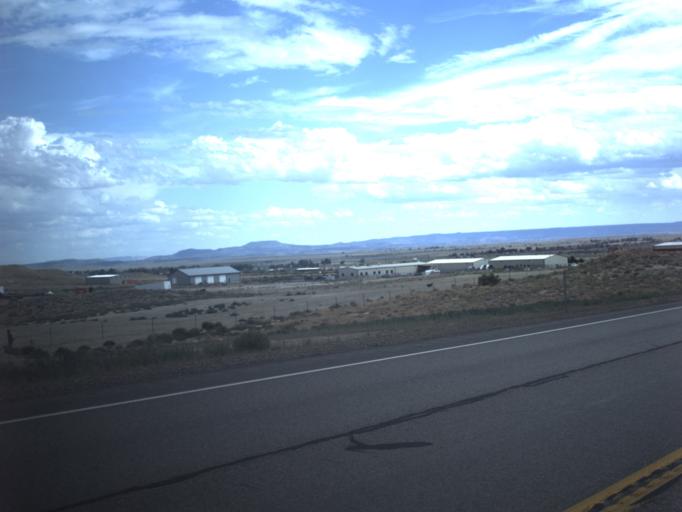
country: US
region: Utah
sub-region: Carbon County
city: Price
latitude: 39.5406
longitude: -110.8146
